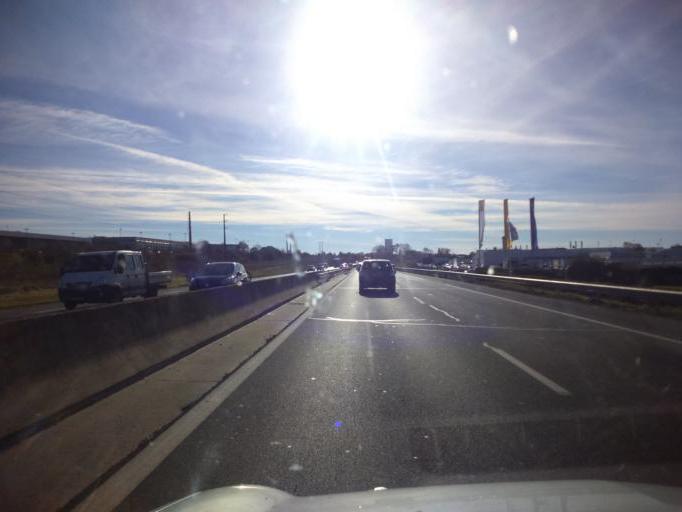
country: FR
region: Poitou-Charentes
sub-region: Departement de la Charente-Maritime
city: Perigny
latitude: 46.1573
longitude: -1.1181
